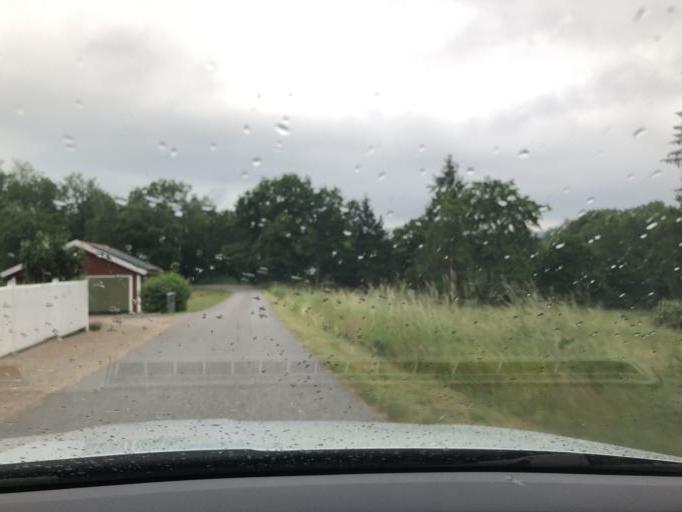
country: SE
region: Blekinge
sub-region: Solvesborgs Kommun
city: Soelvesborg
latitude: 56.1000
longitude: 14.6124
